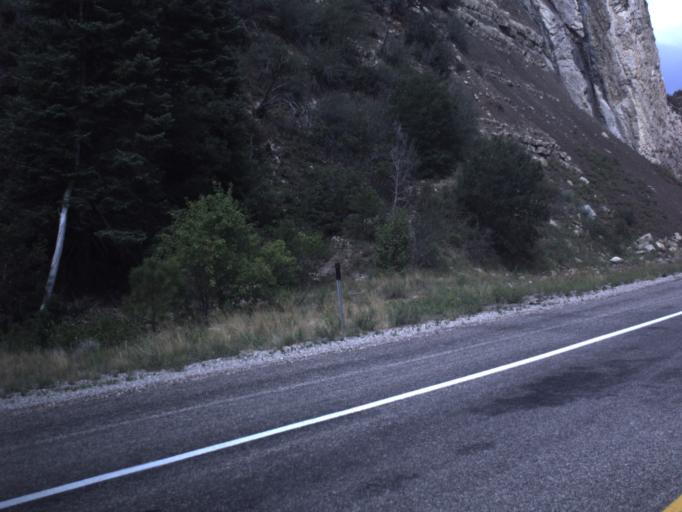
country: US
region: Utah
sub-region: Iron County
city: Cedar City
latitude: 37.6404
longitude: -112.9530
